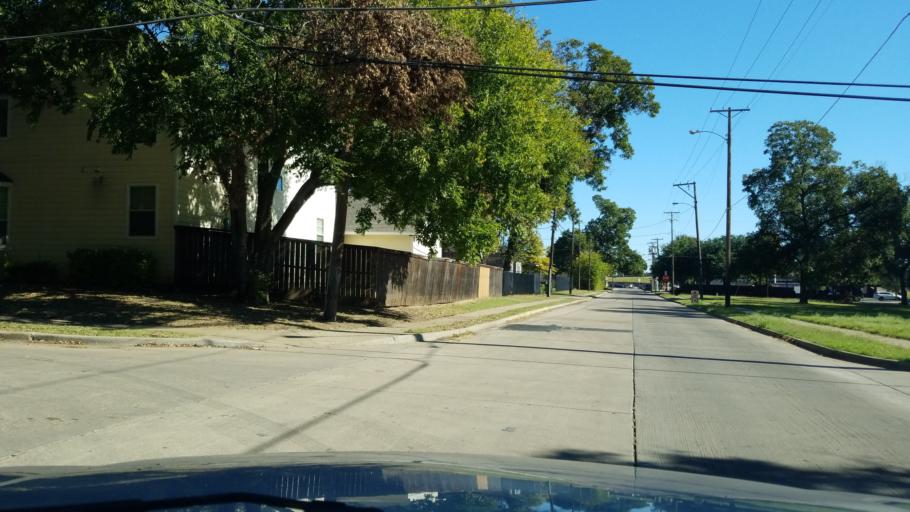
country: US
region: Texas
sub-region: Dallas County
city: Dallas
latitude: 32.7934
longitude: -96.7513
